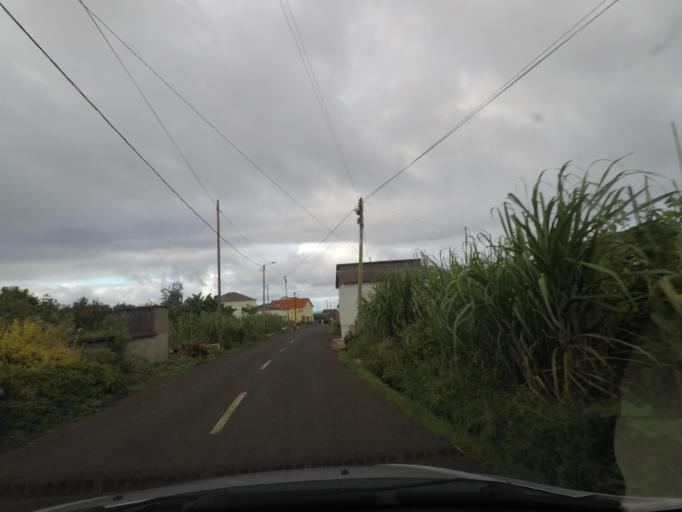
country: PT
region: Madeira
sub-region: Santana
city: Santana
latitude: 32.8140
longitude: -16.8791
